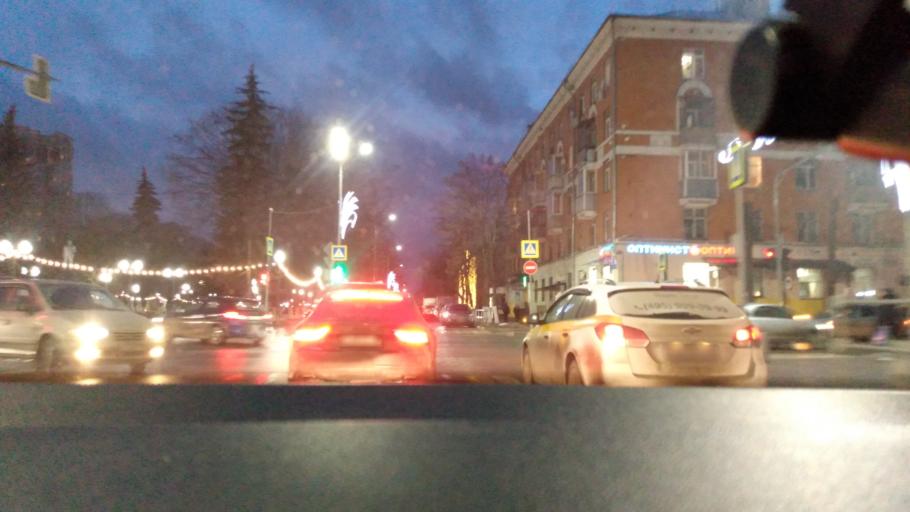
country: RU
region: Moskovskaya
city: Balashikha
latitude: 55.7974
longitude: 37.9349
